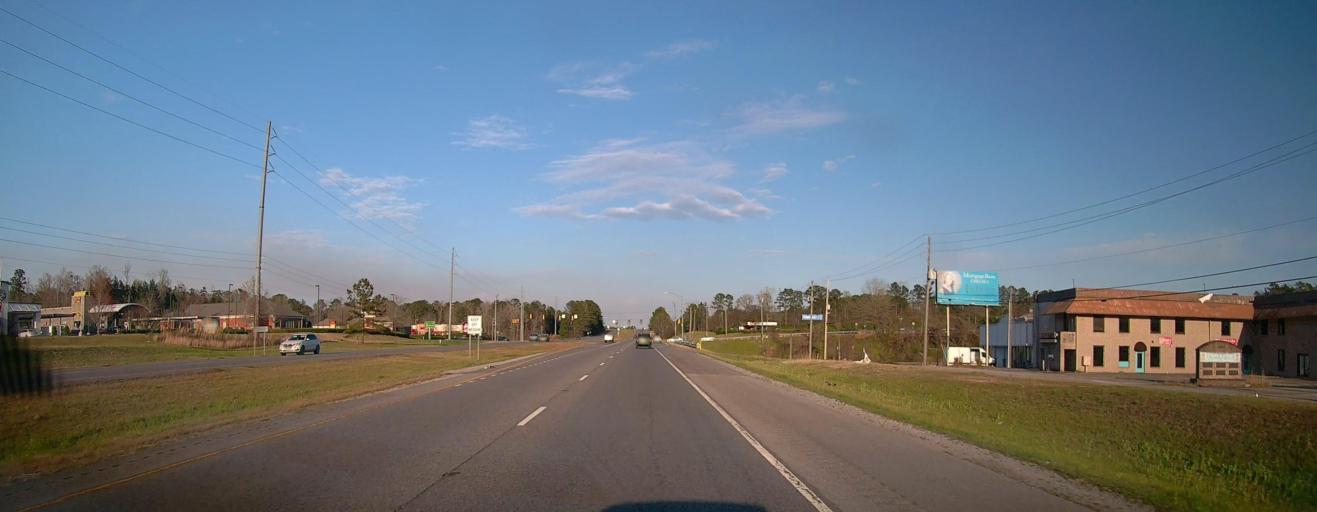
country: US
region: Alabama
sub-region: Shelby County
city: Chelsea
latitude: 33.3494
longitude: -86.6225
